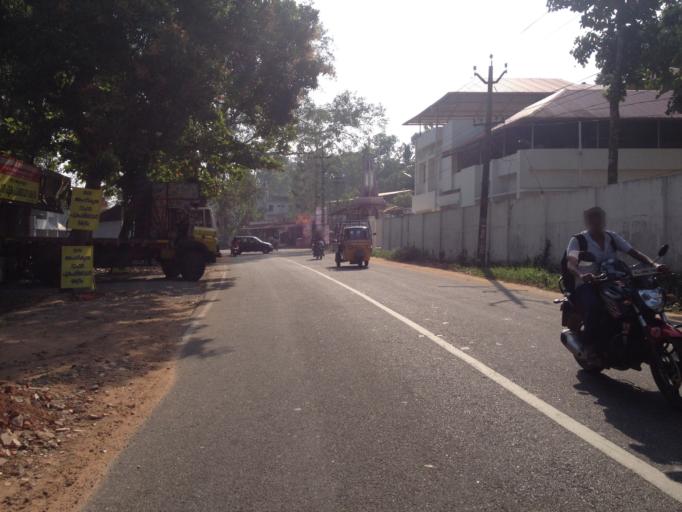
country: IN
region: Kerala
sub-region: Pattanamtitta
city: Adur
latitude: 9.1501
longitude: 76.7497
